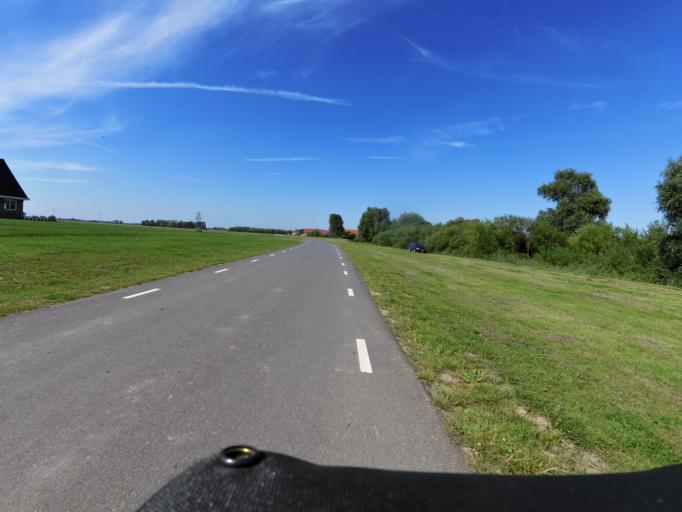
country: NL
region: North Brabant
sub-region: Gemeente Werkendam
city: Werkendam
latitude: 51.7676
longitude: 4.8582
